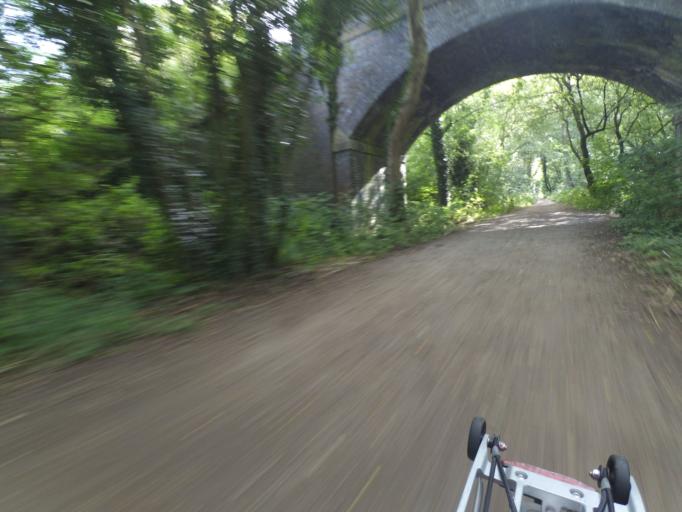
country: GB
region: England
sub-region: Staffordshire
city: Gnosall
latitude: 52.7817
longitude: -2.2765
